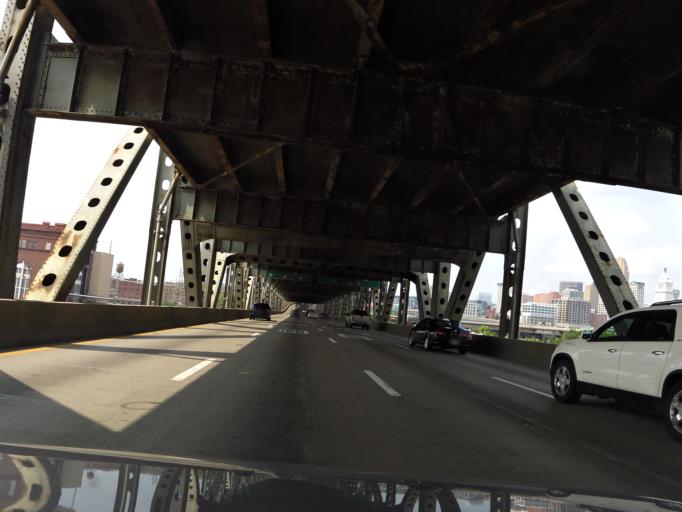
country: US
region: Kentucky
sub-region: Kenton County
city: Covington
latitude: 39.0913
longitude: -84.5225
